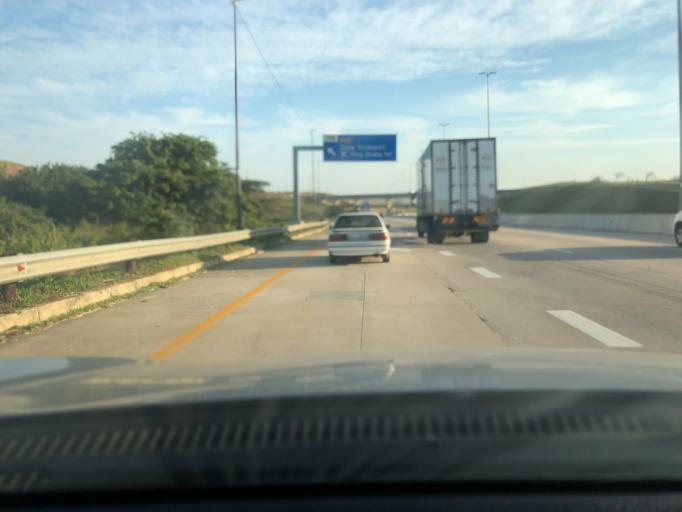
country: ZA
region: KwaZulu-Natal
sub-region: iLembe District Municipality
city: Ballitoville
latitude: -29.6266
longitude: 31.1241
